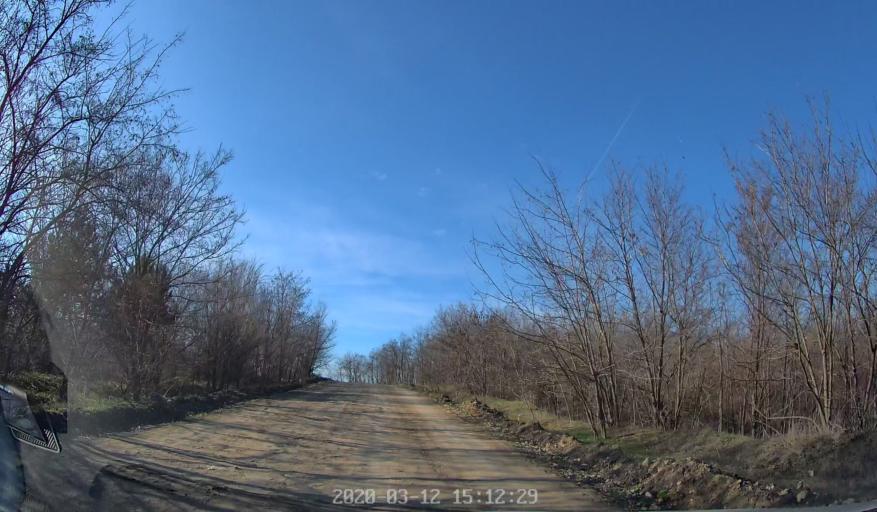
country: MD
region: Chisinau
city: Ciorescu
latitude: 47.2291
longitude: 28.9711
